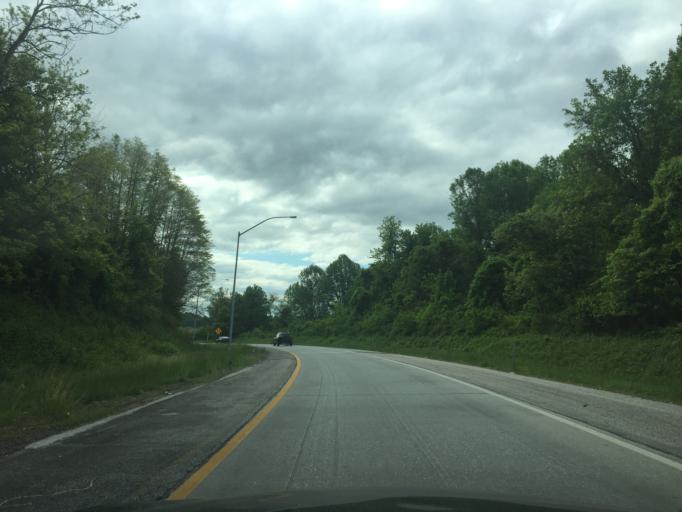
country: US
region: Maryland
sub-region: Baltimore County
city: Owings Mills
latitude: 39.4102
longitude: -76.7937
